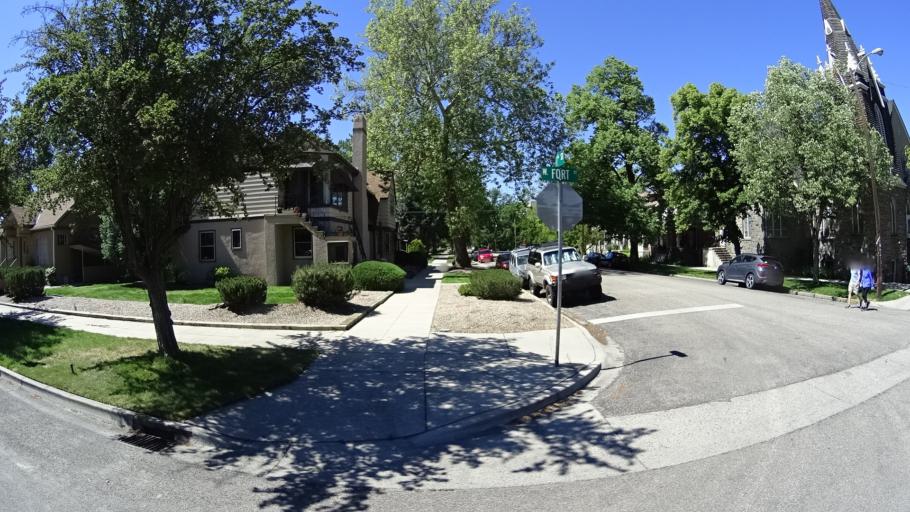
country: US
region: Idaho
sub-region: Ada County
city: Boise
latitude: 43.6211
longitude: -116.1965
